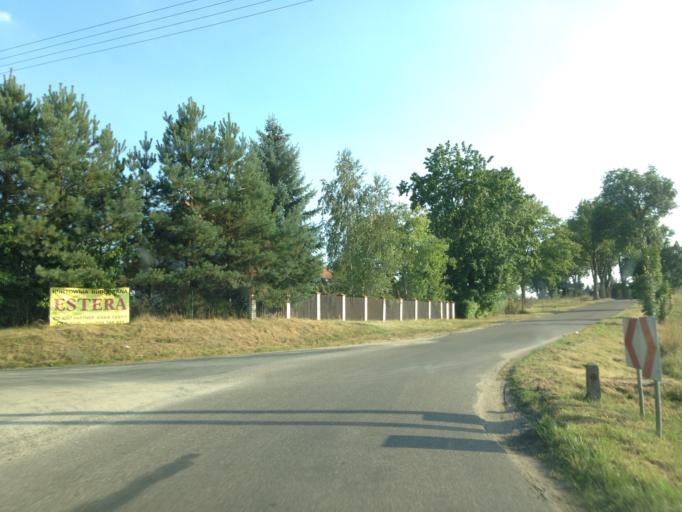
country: PL
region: Warmian-Masurian Voivodeship
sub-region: Powiat nowomiejski
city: Biskupiec
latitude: 53.3855
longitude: 19.3781
